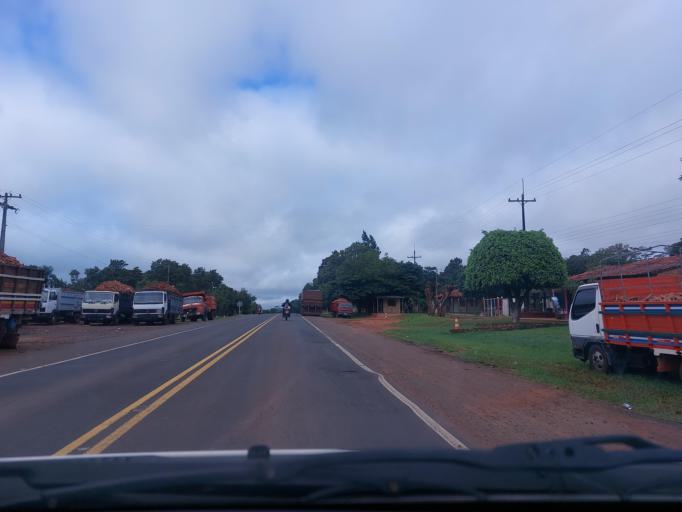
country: PY
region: San Pedro
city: Guayaybi
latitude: -24.5706
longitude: -56.4028
